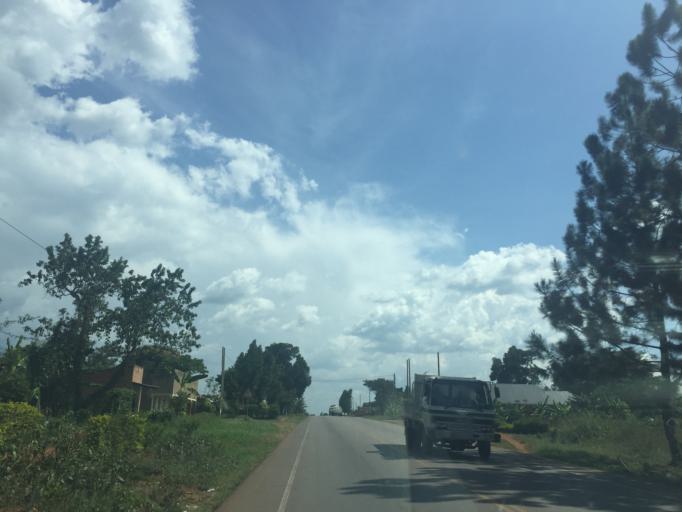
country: UG
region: Central Region
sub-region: Luwero District
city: Wobulenzi
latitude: 0.7847
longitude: 32.5099
